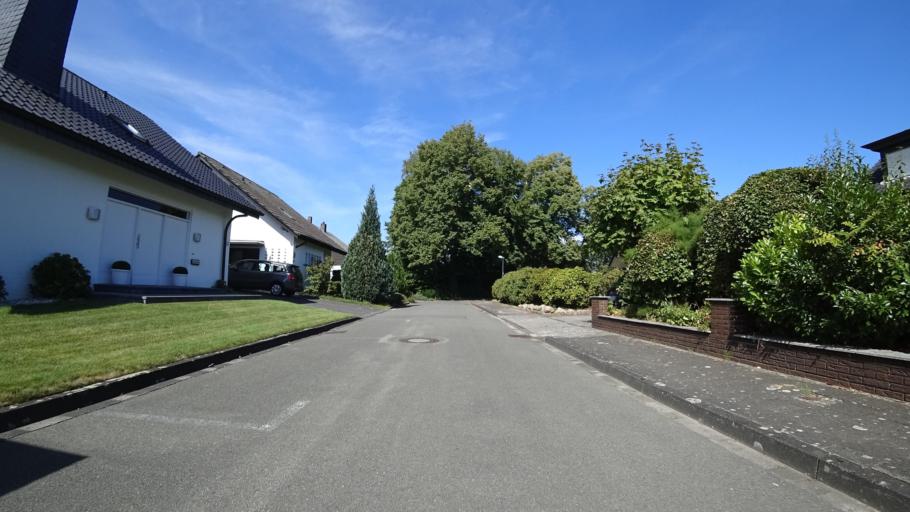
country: DE
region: North Rhine-Westphalia
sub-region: Regierungsbezirk Detmold
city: Guetersloh
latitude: 51.8905
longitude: 8.3993
